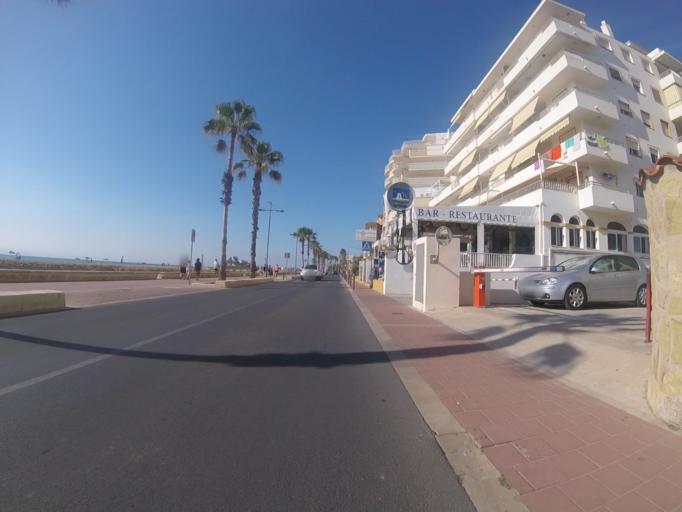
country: ES
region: Valencia
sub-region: Provincia de Castello
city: Peniscola
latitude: 40.3747
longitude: 0.4062
